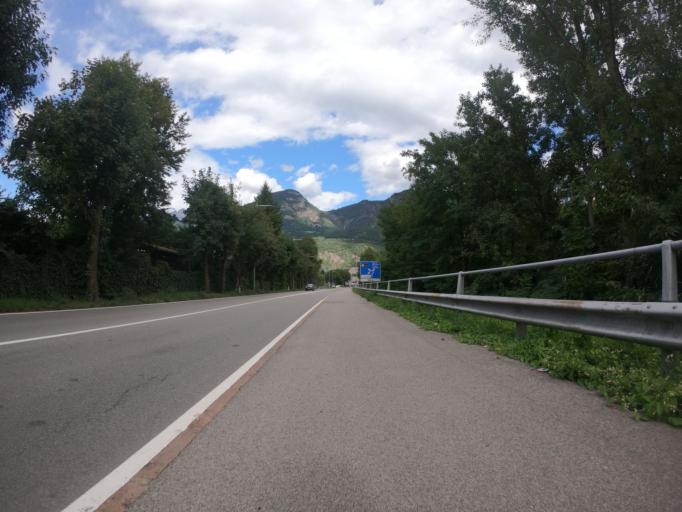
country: IT
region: Trentino-Alto Adige
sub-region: Bolzano
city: Lana
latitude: 46.6278
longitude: 11.1635
